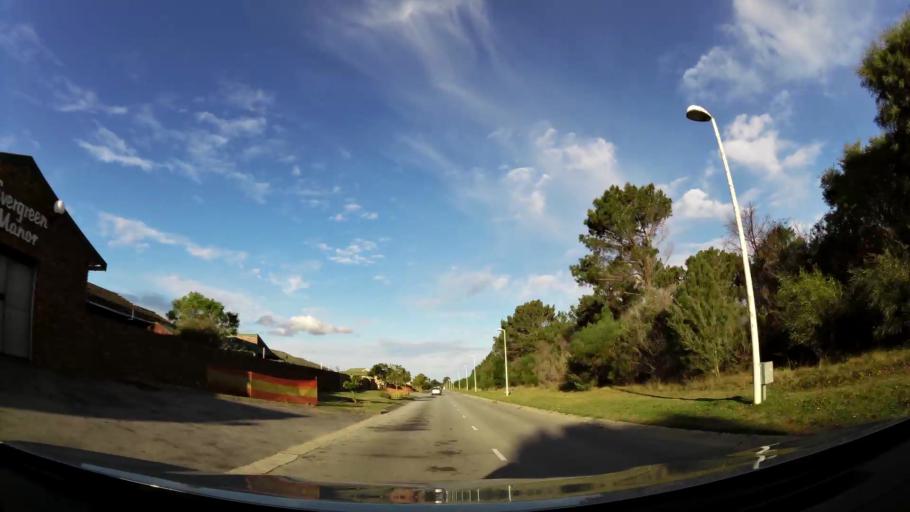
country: ZA
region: Eastern Cape
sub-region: Nelson Mandela Bay Metropolitan Municipality
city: Port Elizabeth
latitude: -33.9768
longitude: 25.5112
